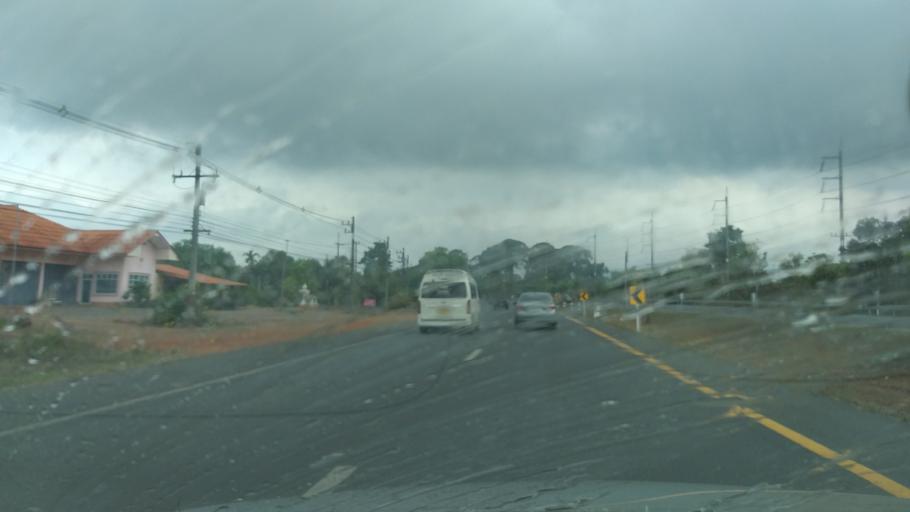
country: TH
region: Chanthaburi
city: Khlung
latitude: 12.4568
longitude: 102.2705
